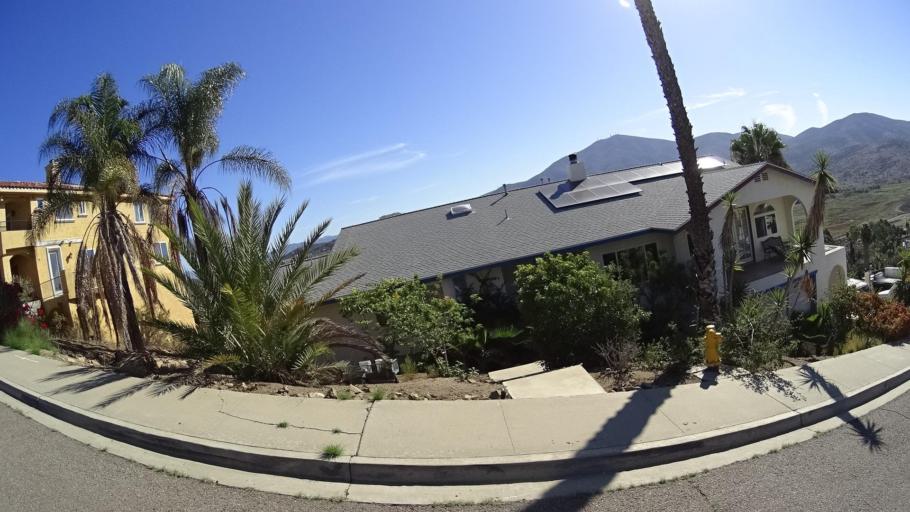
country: US
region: California
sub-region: San Diego County
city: La Presa
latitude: 32.7156
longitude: -116.9843
